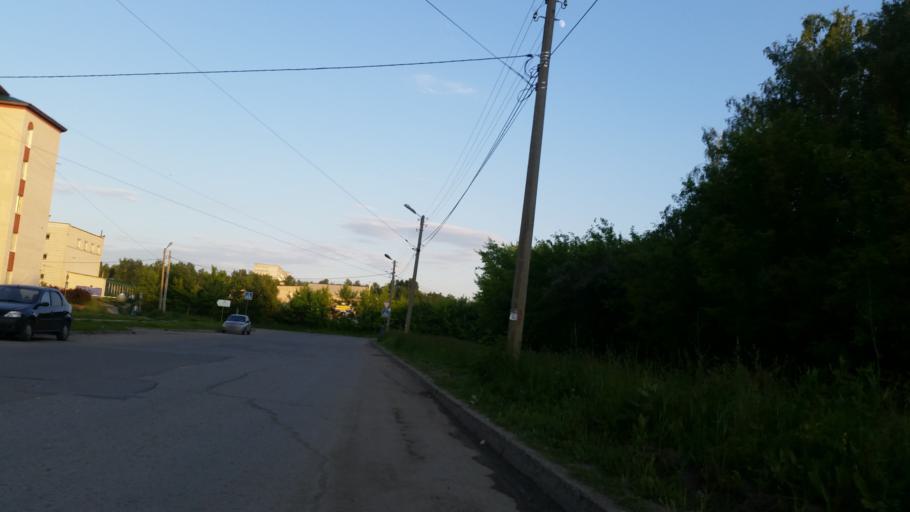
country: RU
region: Ulyanovsk
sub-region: Ulyanovskiy Rayon
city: Ulyanovsk
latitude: 54.3556
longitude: 48.3843
